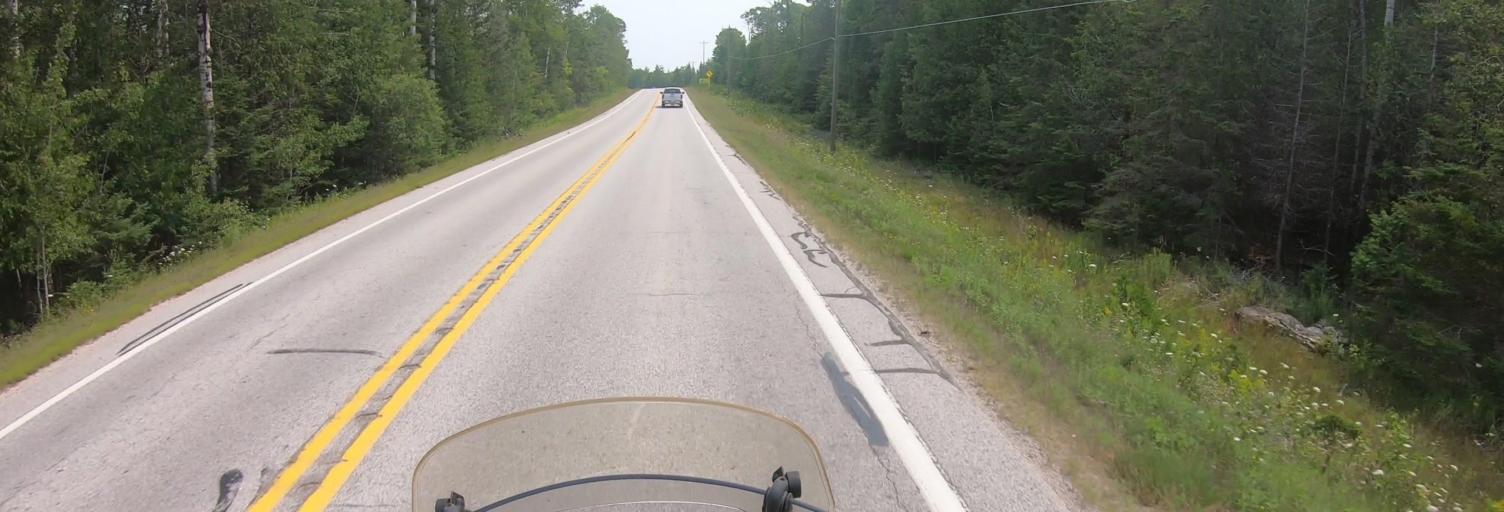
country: CA
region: Ontario
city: Thessalon
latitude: 45.9826
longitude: -83.7968
